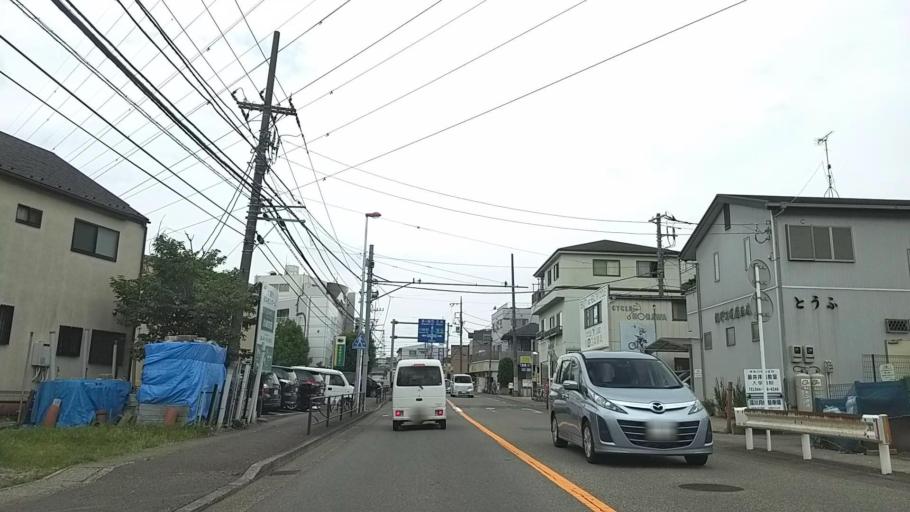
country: JP
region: Tokyo
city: Chofugaoka
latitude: 35.5743
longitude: 139.6197
